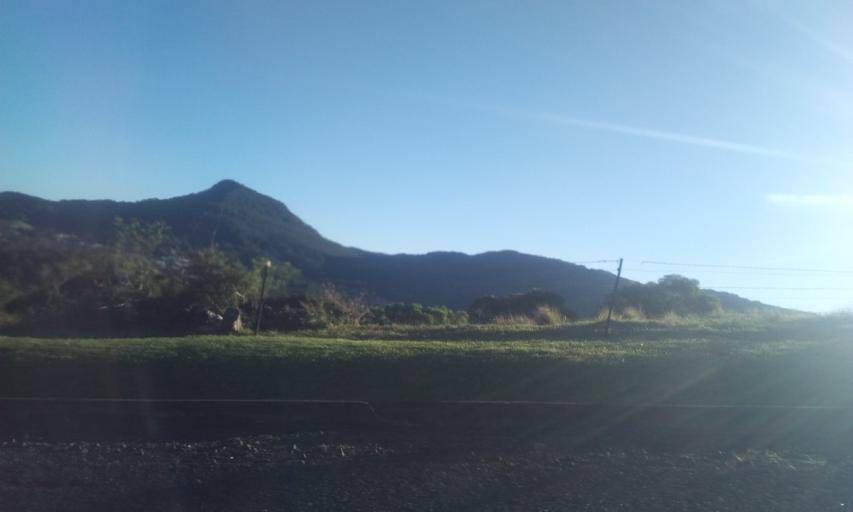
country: AU
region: New South Wales
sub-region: Wollongong
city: Mount Keira
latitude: -34.4259
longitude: 150.8422
